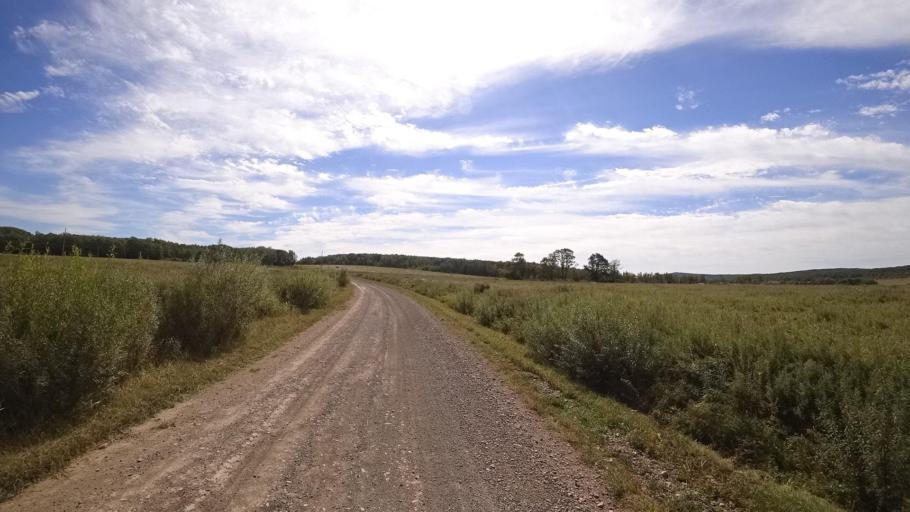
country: RU
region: Primorskiy
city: Yakovlevka
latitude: 44.7134
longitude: 133.6200
